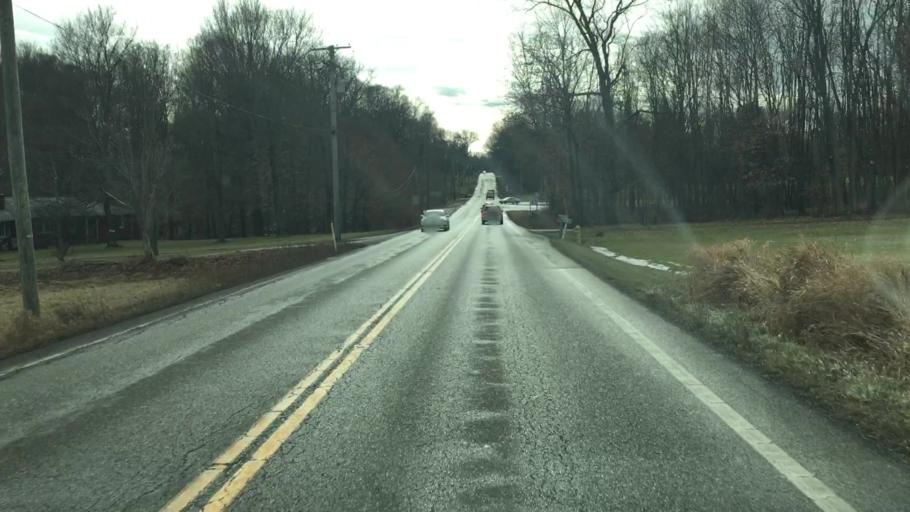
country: US
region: Ohio
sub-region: Columbiana County
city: Salem
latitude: 40.9256
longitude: -80.8404
